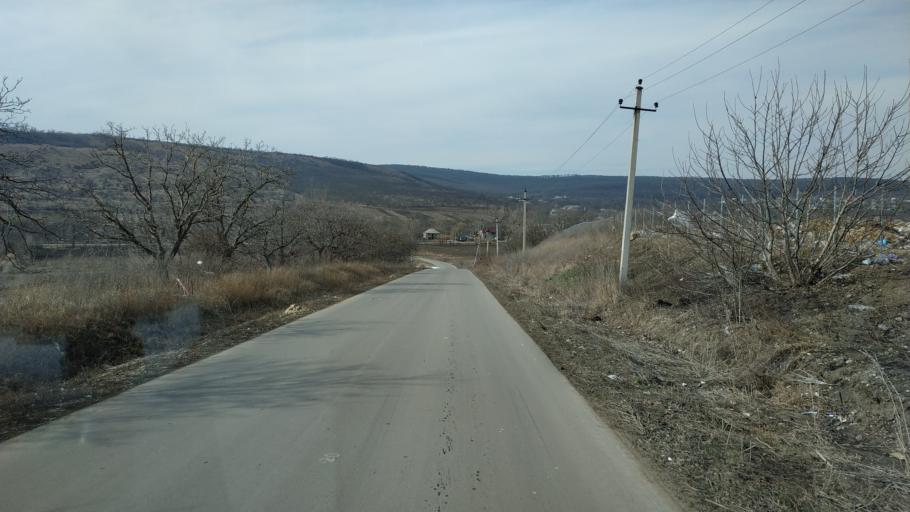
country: MD
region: Nisporeni
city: Nisporeni
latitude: 47.1472
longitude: 28.1149
